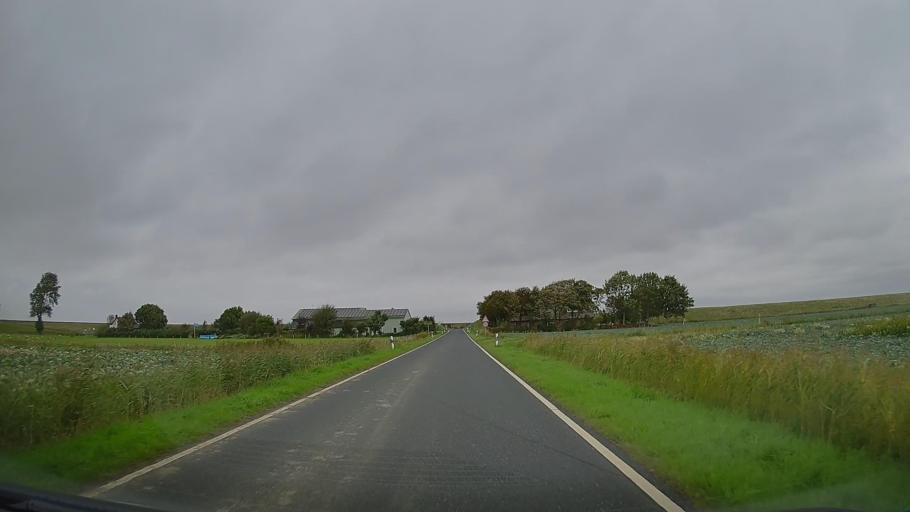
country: DE
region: Schleswig-Holstein
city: Friedrichskoog
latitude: 54.0232
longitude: 8.9144
